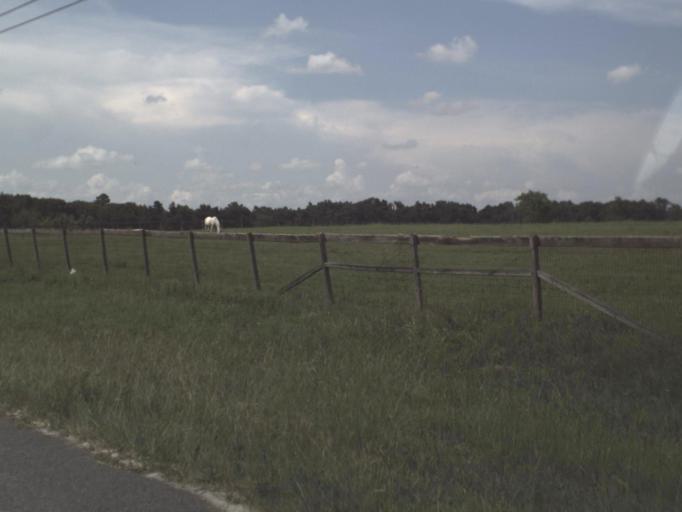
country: US
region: Florida
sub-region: Citrus County
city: Hernando
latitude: 28.9417
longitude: -82.4010
